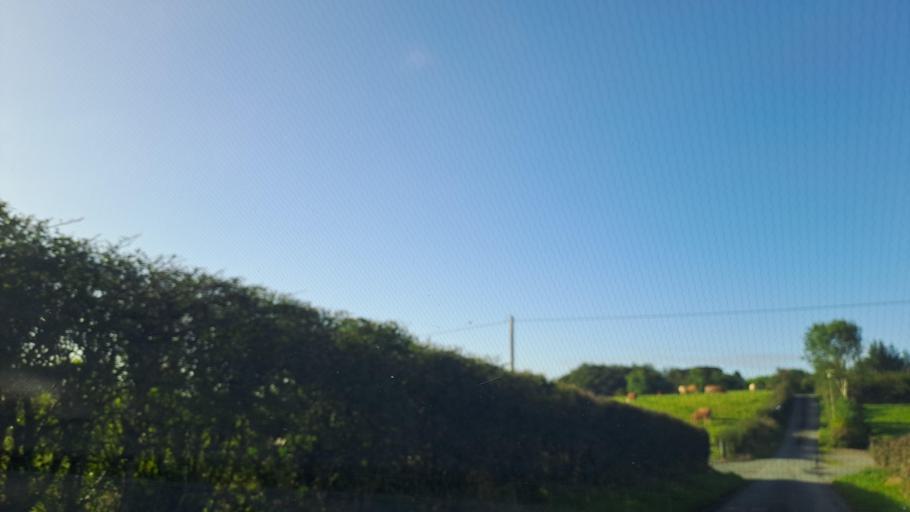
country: IE
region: Ulster
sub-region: An Cabhan
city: Kingscourt
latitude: 53.9538
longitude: -6.8729
